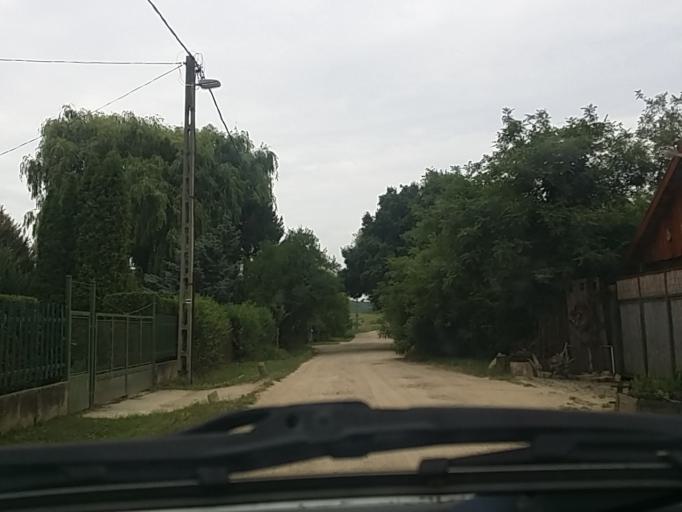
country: HU
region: Pest
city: Pilisborosjeno
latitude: 47.6055
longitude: 18.9627
